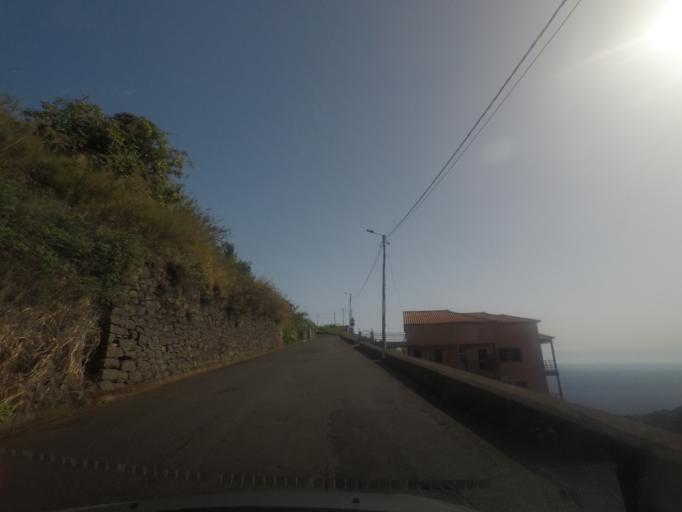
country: PT
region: Madeira
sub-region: Calheta
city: Arco da Calheta
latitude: 32.7282
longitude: -17.1604
